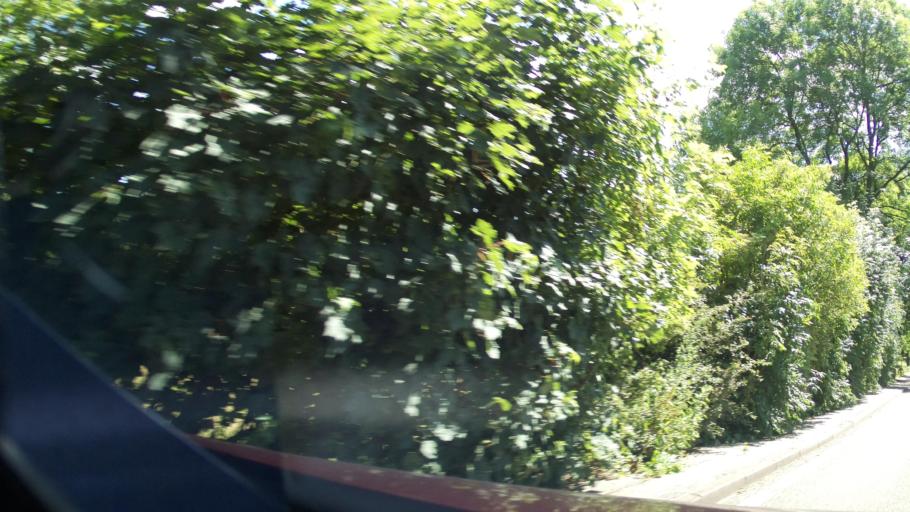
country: GB
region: England
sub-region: Derbyshire
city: Ashbourne
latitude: 53.0517
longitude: -1.7415
